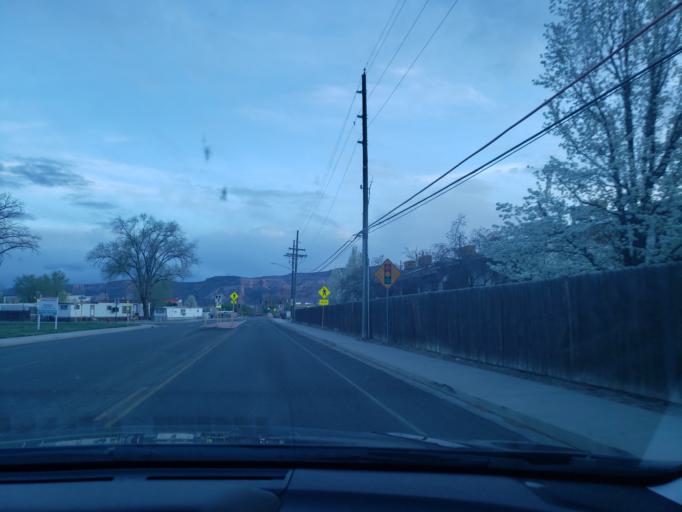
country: US
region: Colorado
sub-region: Mesa County
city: Fruita
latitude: 39.1505
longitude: -108.7198
